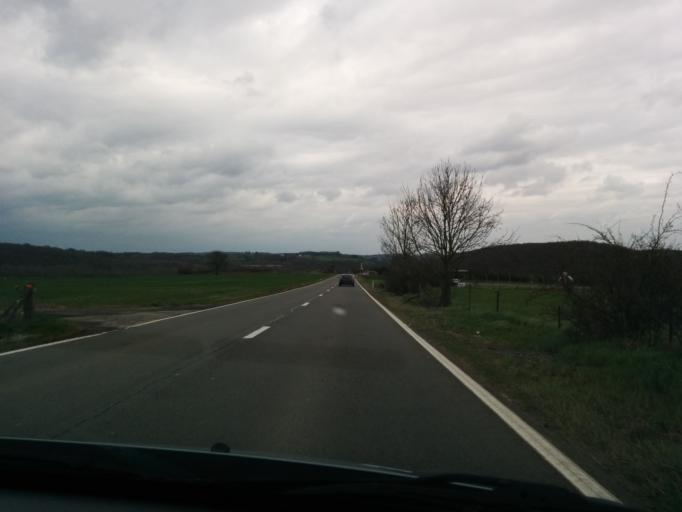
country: BE
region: Wallonia
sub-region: Province de Namur
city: Floreffe
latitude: 50.4094
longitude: 4.7447
